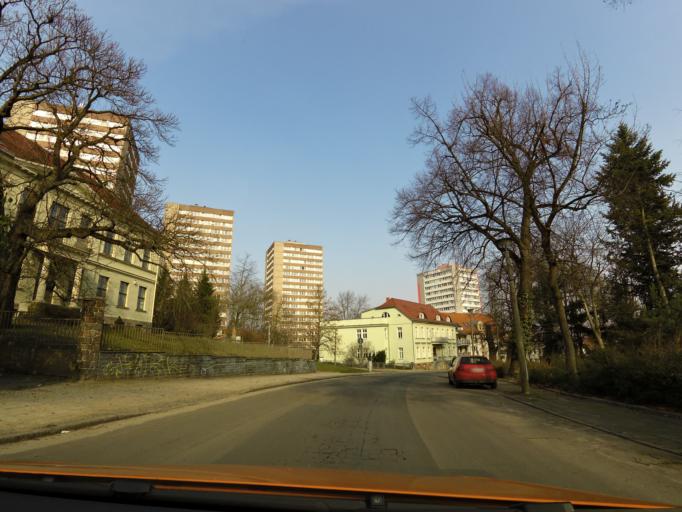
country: DE
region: Brandenburg
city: Frankfurt (Oder)
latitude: 52.3496
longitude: 14.5471
